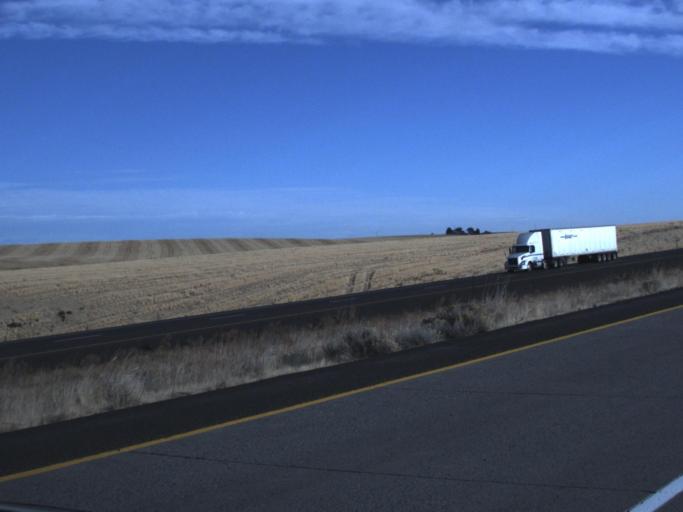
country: US
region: Washington
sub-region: Adams County
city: Ritzville
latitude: 46.9244
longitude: -118.5964
